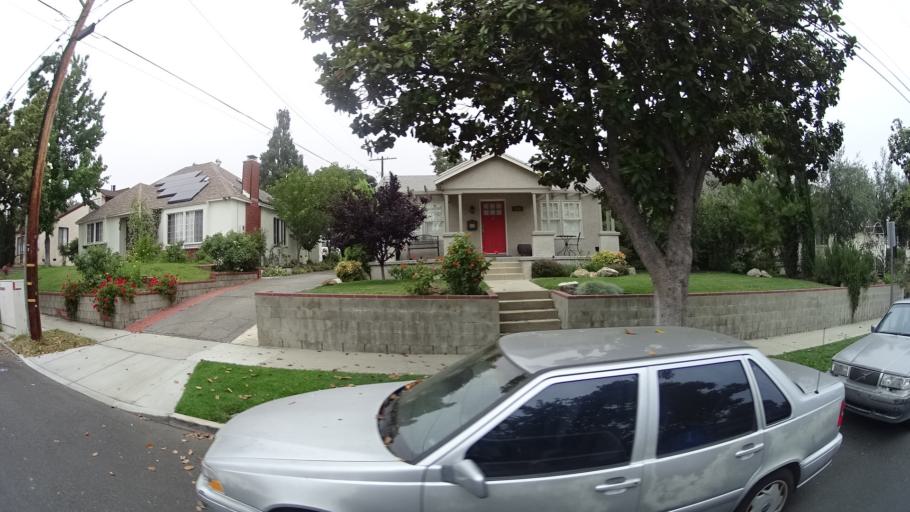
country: US
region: California
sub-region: Los Angeles County
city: Burbank
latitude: 34.1854
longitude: -118.2978
